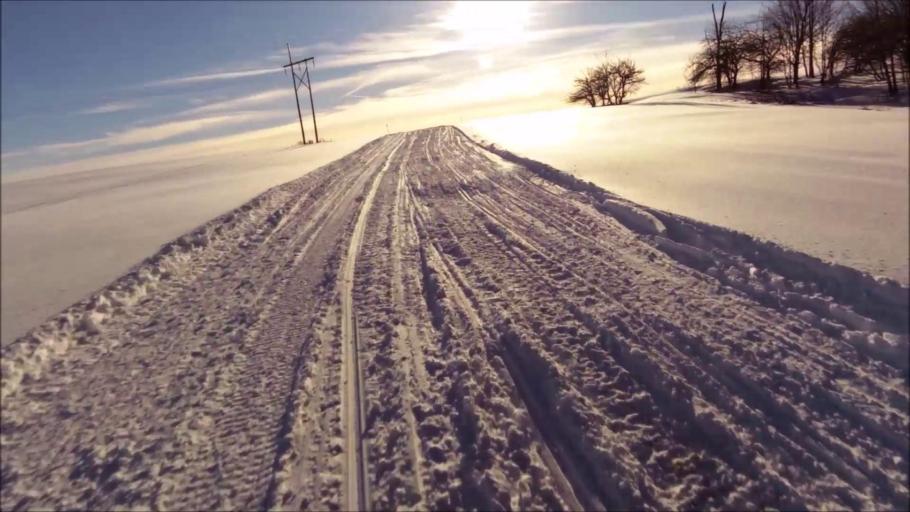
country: US
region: New York
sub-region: Chautauqua County
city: Mayville
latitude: 42.2632
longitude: -79.3844
